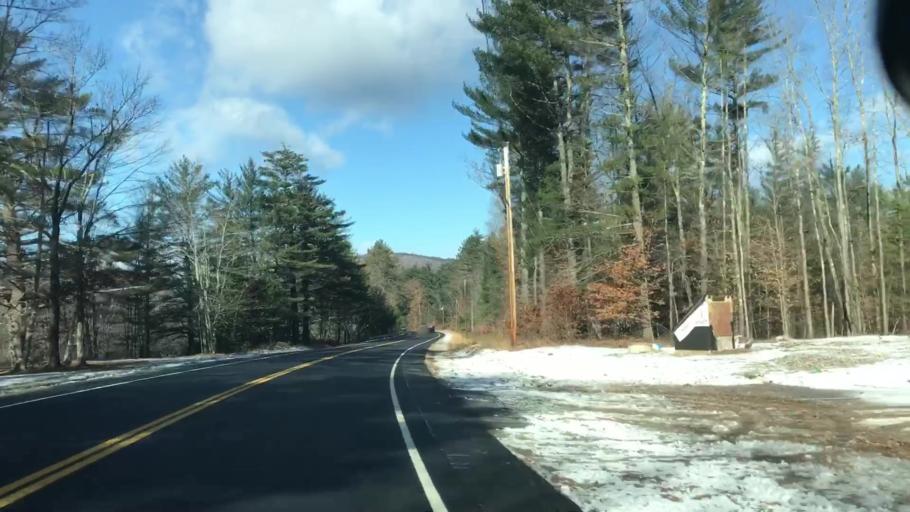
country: US
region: New Hampshire
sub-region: Carroll County
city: Effingham
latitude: 43.7898
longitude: -70.9765
